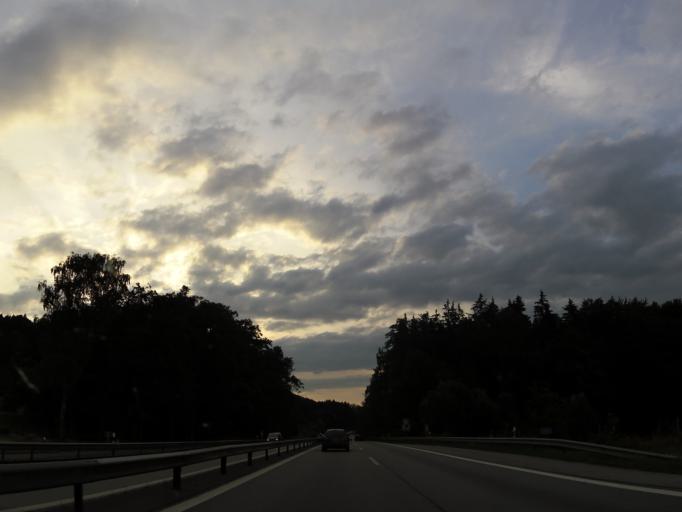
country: DE
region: Bavaria
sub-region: Upper Bavaria
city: Anger
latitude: 47.8082
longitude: 12.8409
